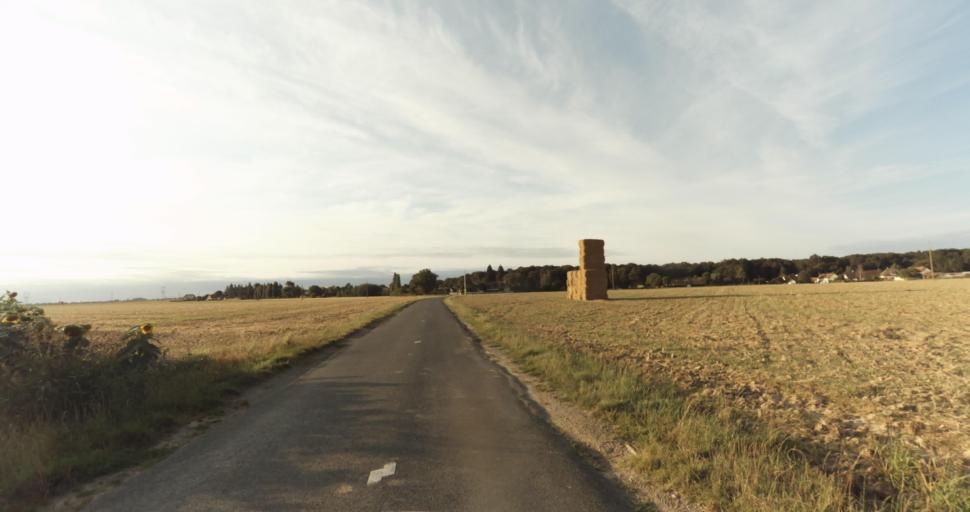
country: FR
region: Haute-Normandie
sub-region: Departement de l'Eure
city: Marcilly-sur-Eure
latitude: 48.8420
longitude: 1.2787
